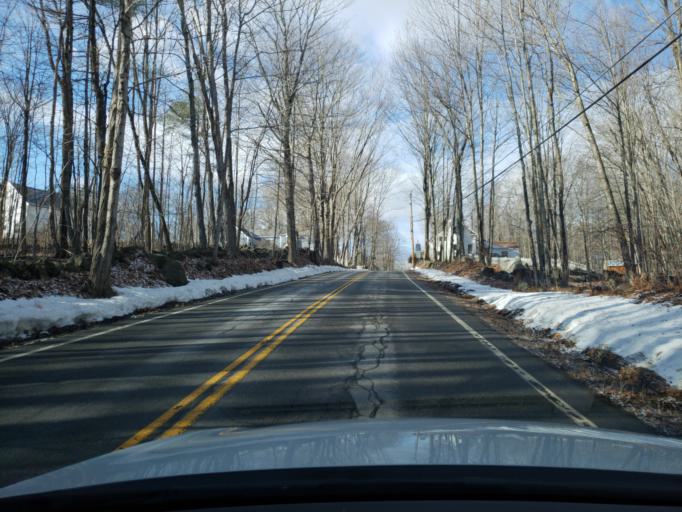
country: US
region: New Hampshire
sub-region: Hillsborough County
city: Greenfield
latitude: 42.9865
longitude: -71.8086
